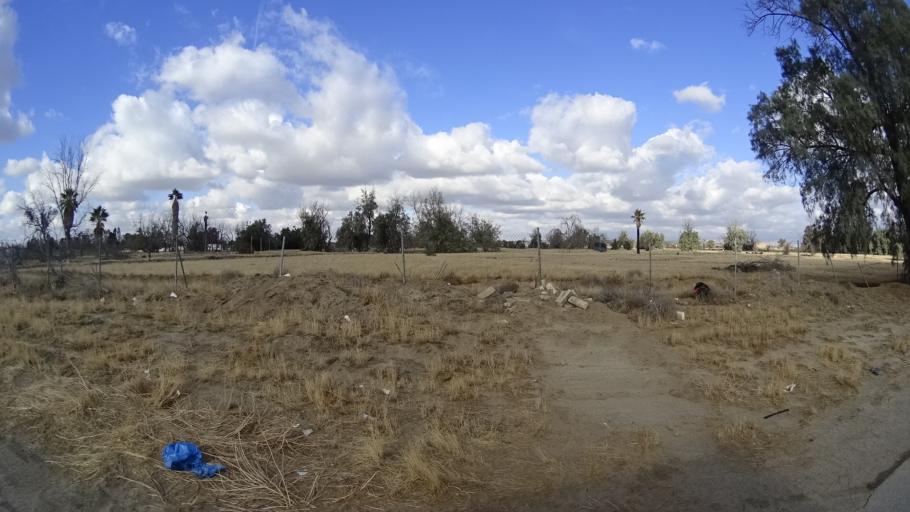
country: US
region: California
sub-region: Kern County
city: Bakersfield
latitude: 35.3322
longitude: -118.9822
